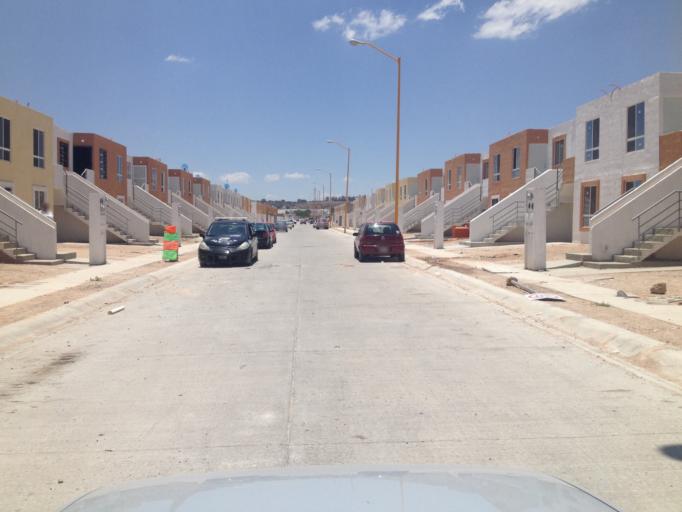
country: MX
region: Aguascalientes
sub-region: Aguascalientes
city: San Sebastian [Fraccionamiento]
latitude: 21.8065
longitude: -102.2752
